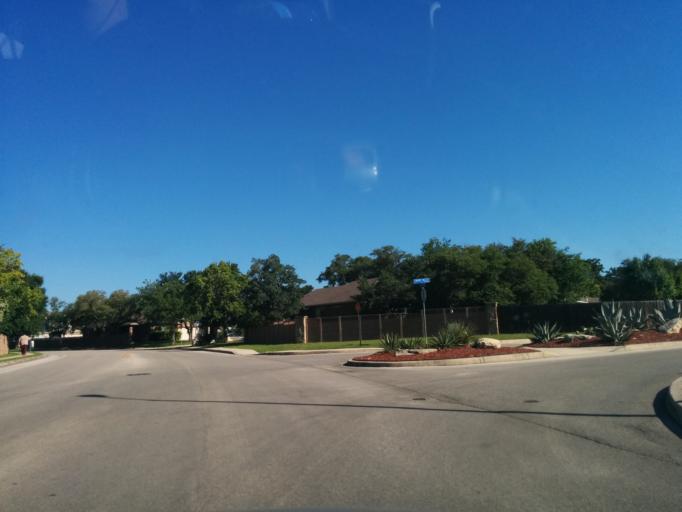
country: US
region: Texas
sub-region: Bexar County
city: Cross Mountain
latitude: 29.6713
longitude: -98.6415
